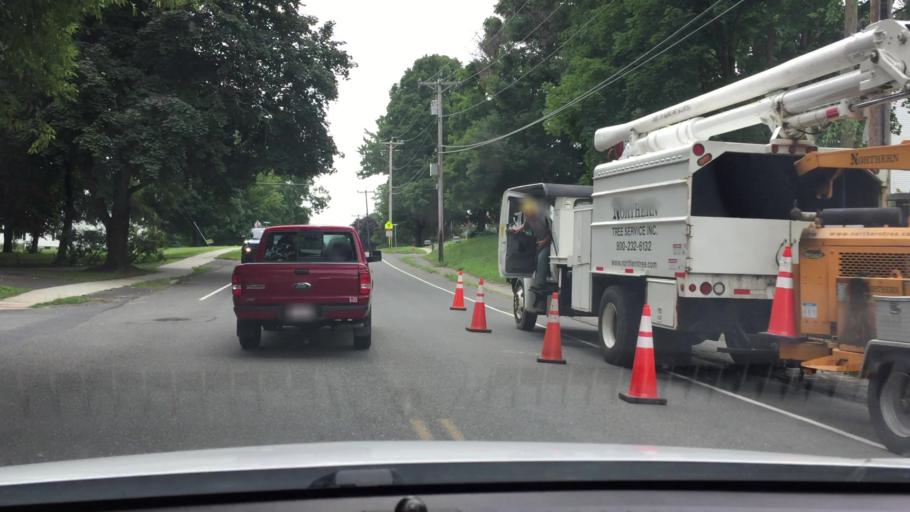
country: US
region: Massachusetts
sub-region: Berkshire County
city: Pittsfield
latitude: 42.4394
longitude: -73.2358
